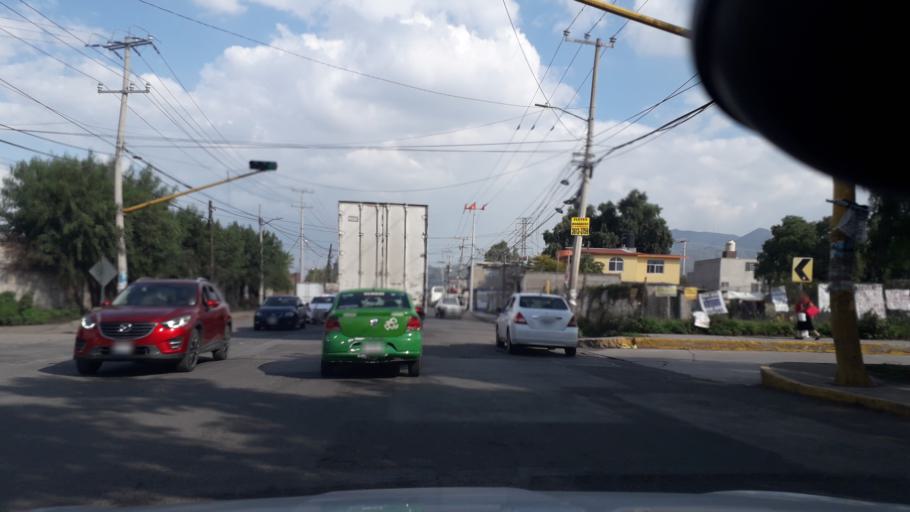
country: MX
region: Mexico
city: Tultitlan
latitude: 19.6316
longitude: -99.1735
